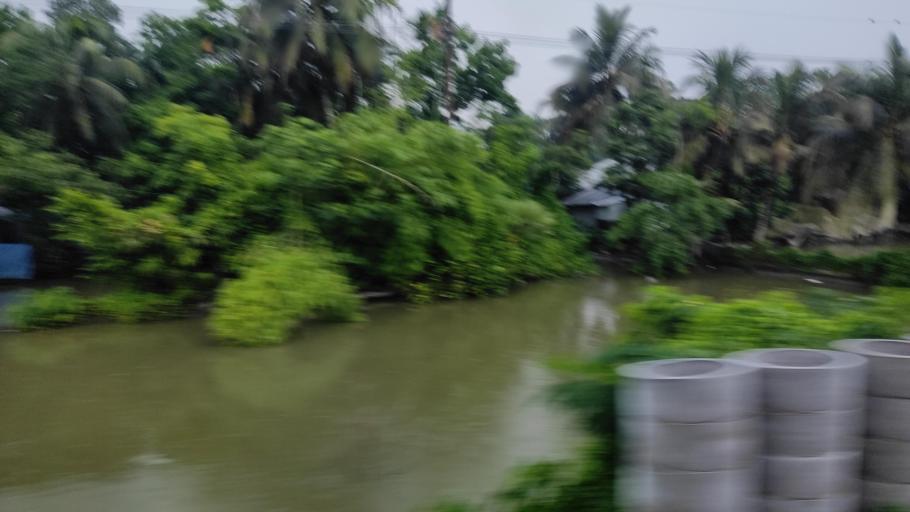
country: BD
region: Barisal
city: Bhandaria
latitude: 22.3150
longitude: 90.3254
